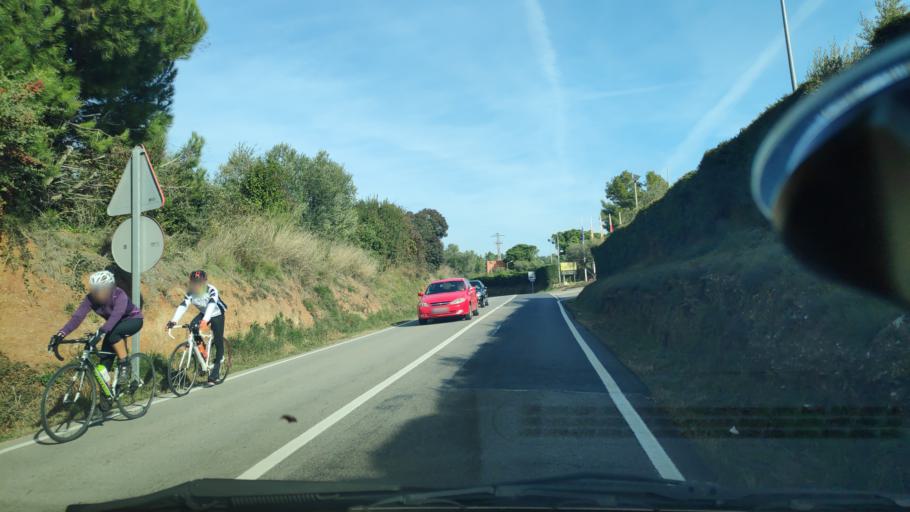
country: ES
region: Catalonia
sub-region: Provincia de Barcelona
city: Matadepera
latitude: 41.5953
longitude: 2.0386
